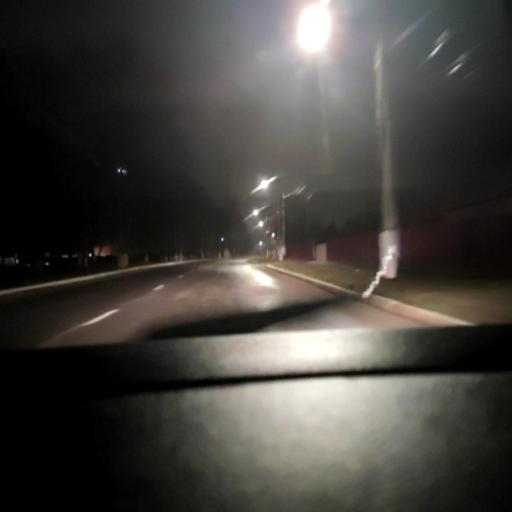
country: RU
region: Voronezj
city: Semiluki
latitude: 51.6910
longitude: 39.0362
